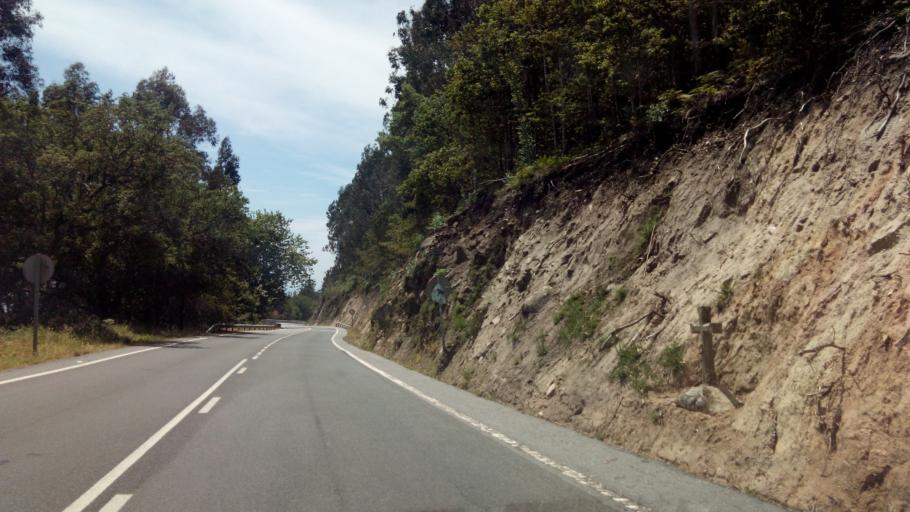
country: ES
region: Galicia
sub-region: Provincia de Pontevedra
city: Moana
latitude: 42.3176
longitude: -8.7244
